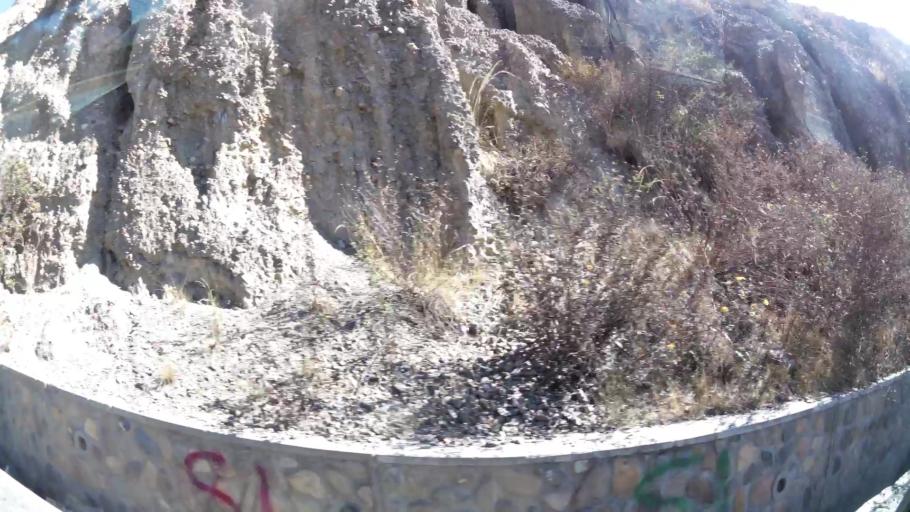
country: BO
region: La Paz
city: La Paz
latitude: -16.5196
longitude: -68.1430
